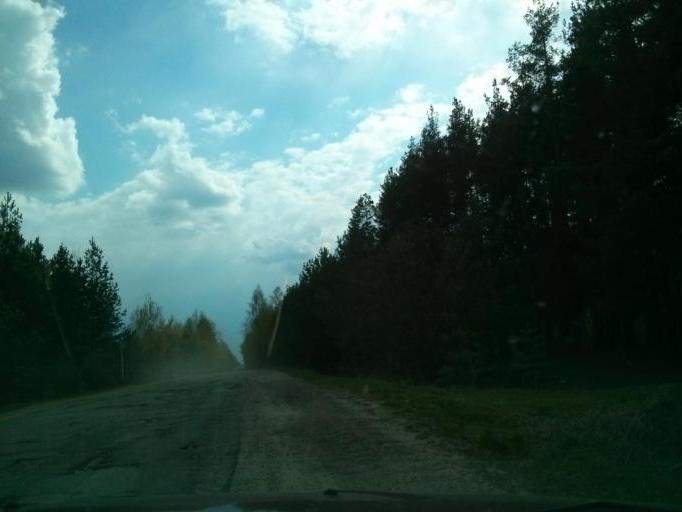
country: RU
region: Nizjnij Novgorod
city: Shimorskoye
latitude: 55.4516
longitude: 41.9810
